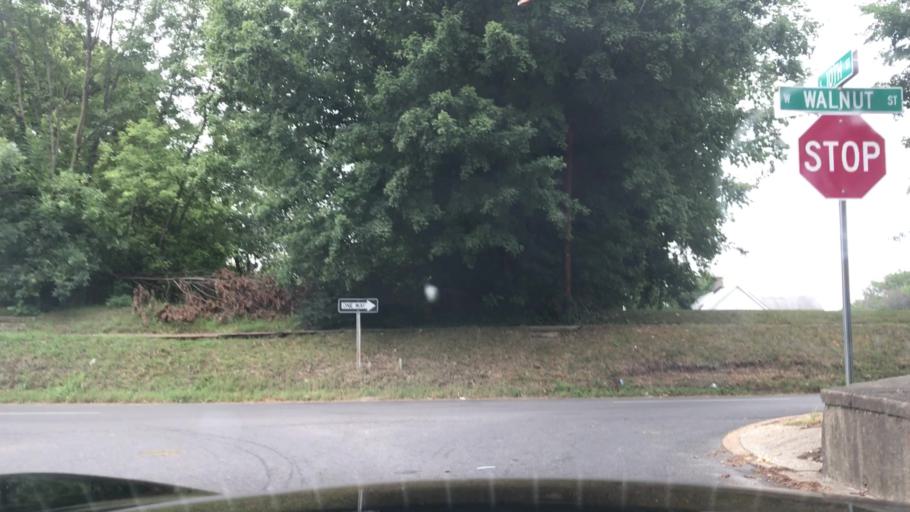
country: US
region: Kentucky
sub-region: Graves County
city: Mayfield
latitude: 36.7382
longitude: -88.6411
